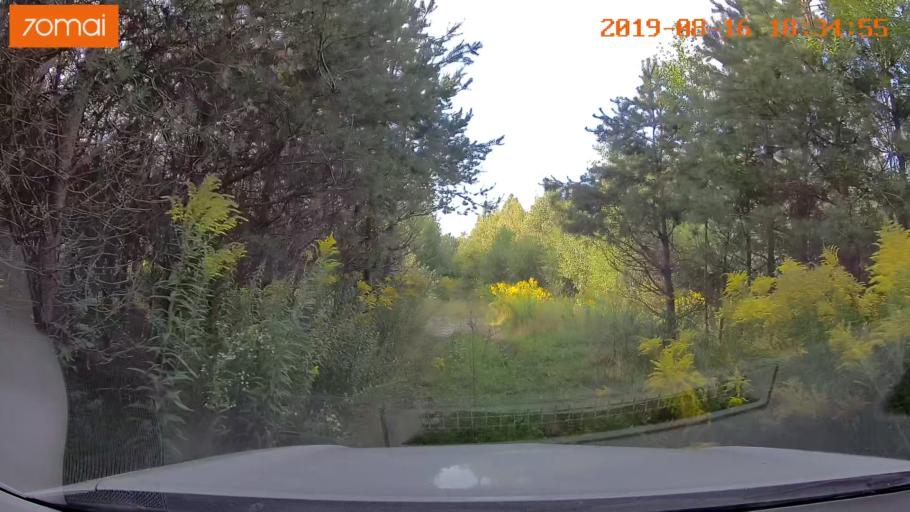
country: BY
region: Mogilev
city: Asipovichy
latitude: 53.2040
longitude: 28.6375
